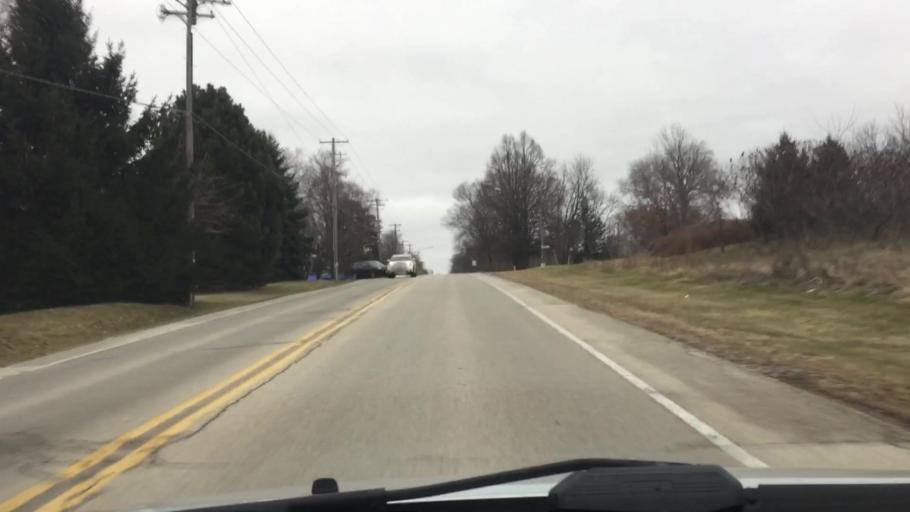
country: US
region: Wisconsin
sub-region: Waukesha County
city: Delafield
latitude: 43.0756
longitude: -88.4036
